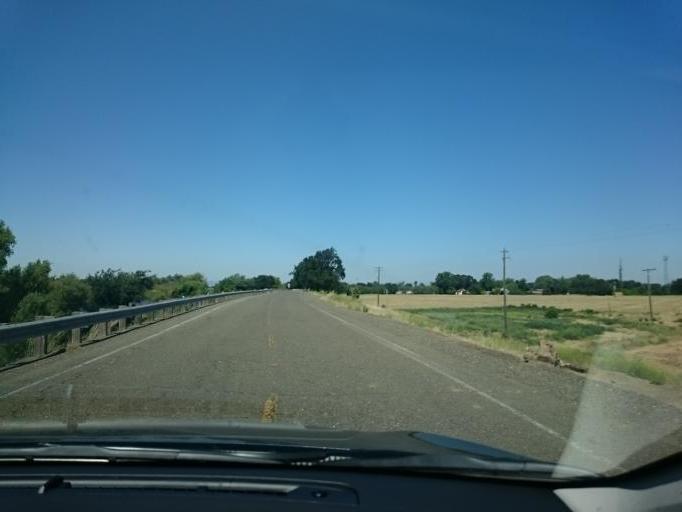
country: US
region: California
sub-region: Yolo County
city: West Sacramento
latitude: 38.5182
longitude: -121.5311
